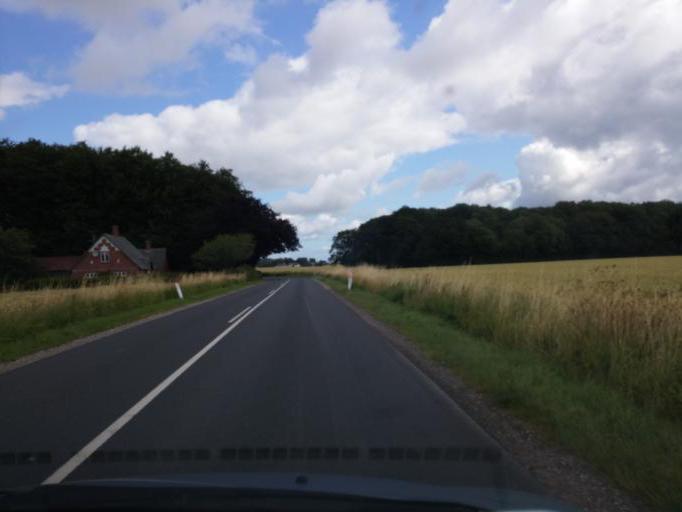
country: DK
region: South Denmark
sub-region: Kerteminde Kommune
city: Kerteminde
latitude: 55.4219
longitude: 10.6140
